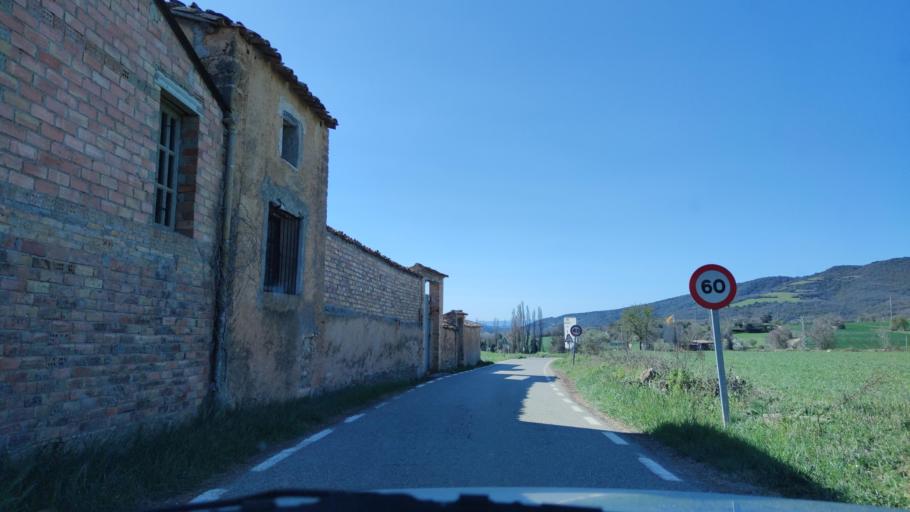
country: ES
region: Catalonia
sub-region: Provincia de Lleida
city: Artesa de Segre
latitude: 41.9908
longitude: 1.0233
